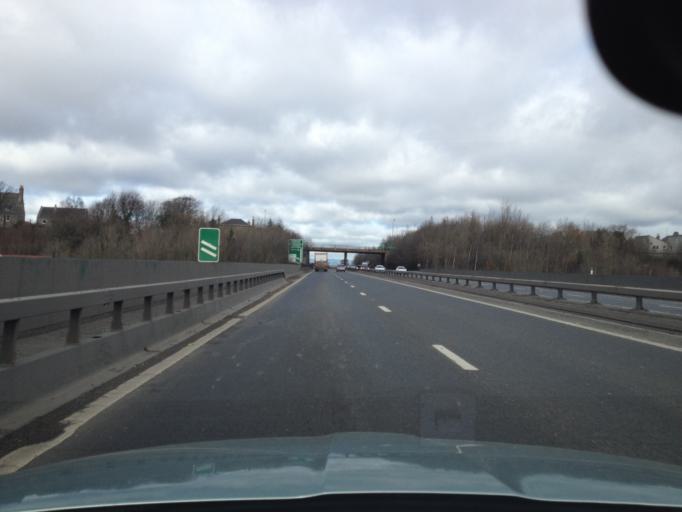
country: GB
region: Scotland
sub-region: Edinburgh
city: Colinton
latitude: 55.9052
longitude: -3.2752
